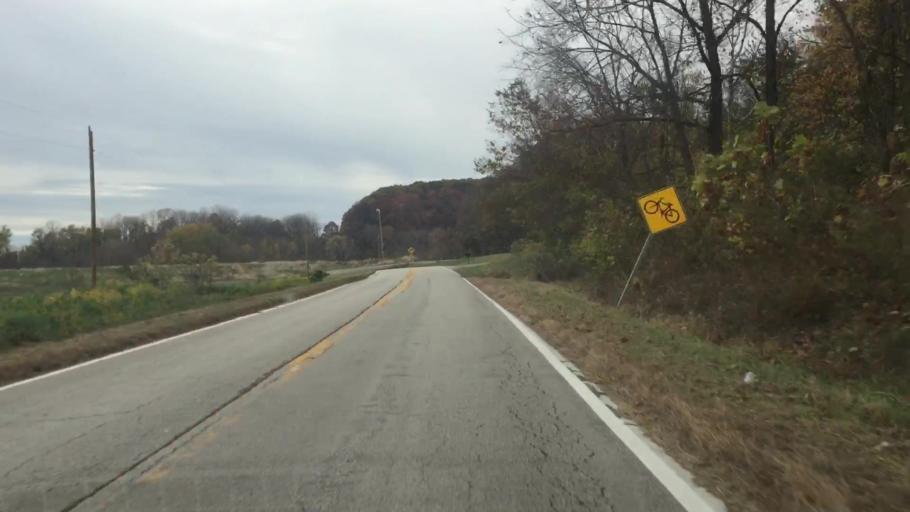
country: US
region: Missouri
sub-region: Gasconade County
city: Hermann
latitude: 38.7053
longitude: -91.6213
